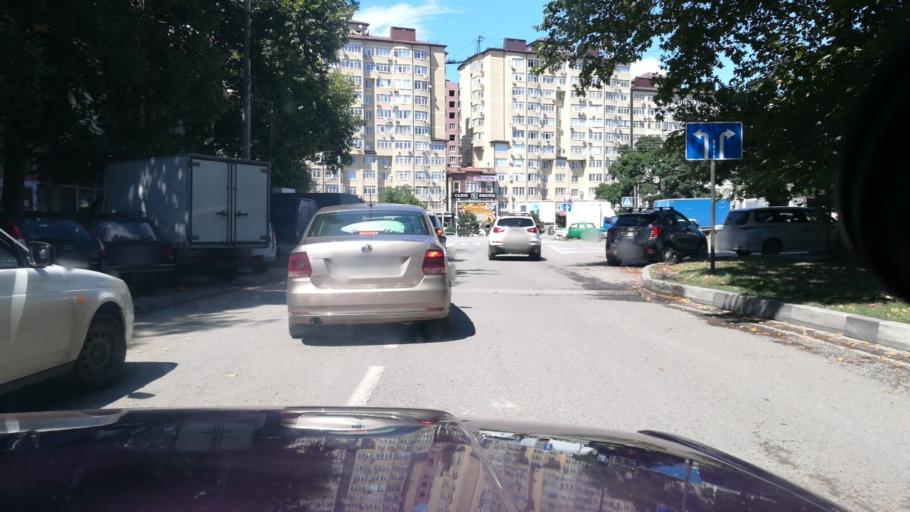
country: RU
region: Krasnodarskiy
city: Anapa
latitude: 44.8986
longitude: 37.3434
